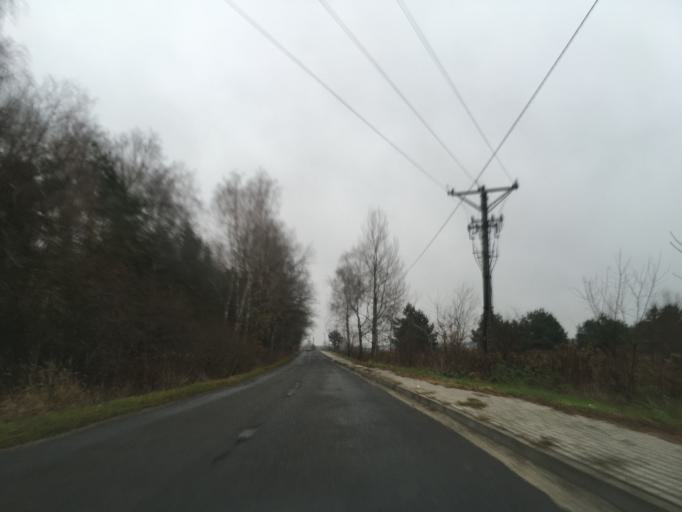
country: PL
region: Masovian Voivodeship
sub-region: Powiat piaseczynski
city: Lesznowola
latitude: 52.0709
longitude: 20.8799
